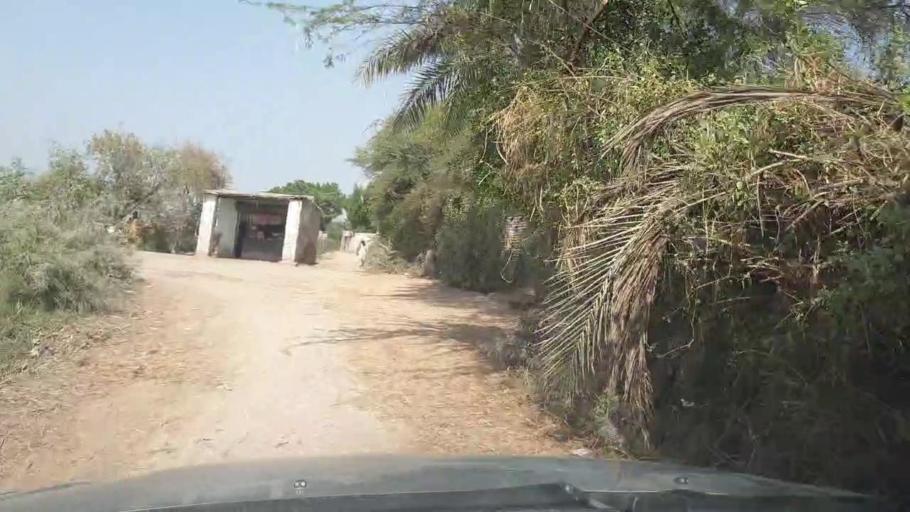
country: PK
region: Sindh
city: Bulri
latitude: 24.8671
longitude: 68.3289
